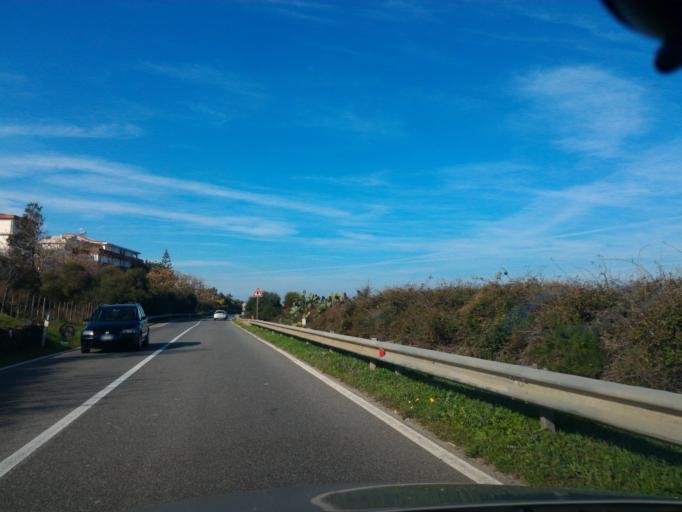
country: IT
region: Calabria
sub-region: Provincia di Crotone
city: Torretta
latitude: 39.4399
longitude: 17.0498
